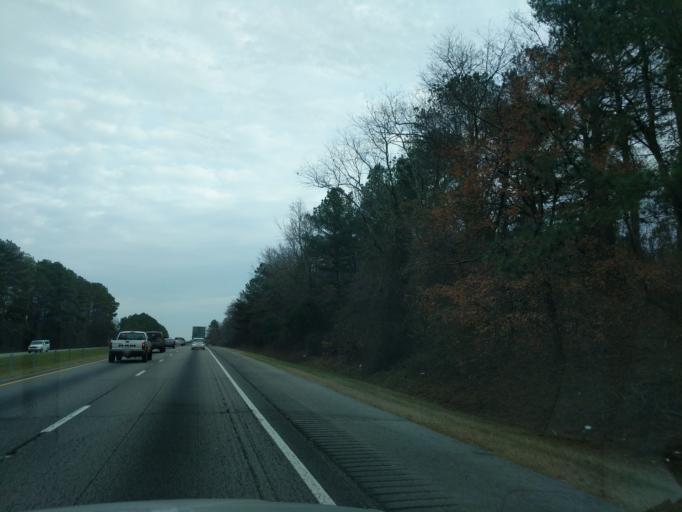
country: US
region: Georgia
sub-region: Jackson County
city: Braselton
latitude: 34.1301
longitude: -83.6970
